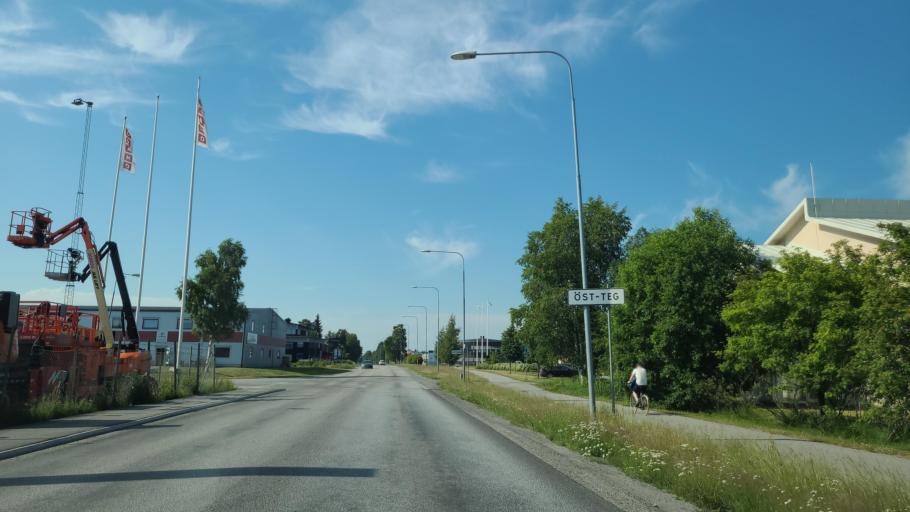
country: SE
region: Vaesterbotten
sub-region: Umea Kommun
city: Umea
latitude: 63.8020
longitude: 20.2794
